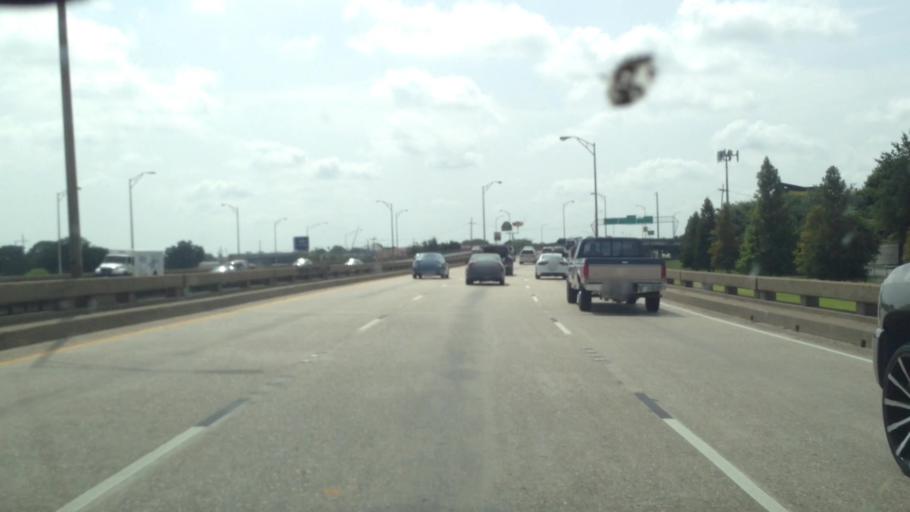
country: US
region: Louisiana
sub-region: Jefferson Parish
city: Kenner
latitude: 30.0069
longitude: -90.2118
